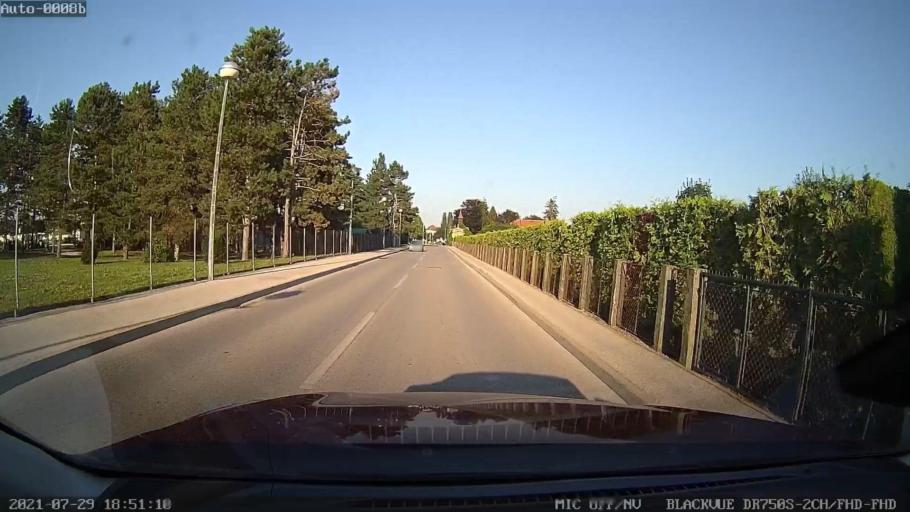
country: HR
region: Varazdinska
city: Varazdin
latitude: 46.3104
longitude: 16.3233
